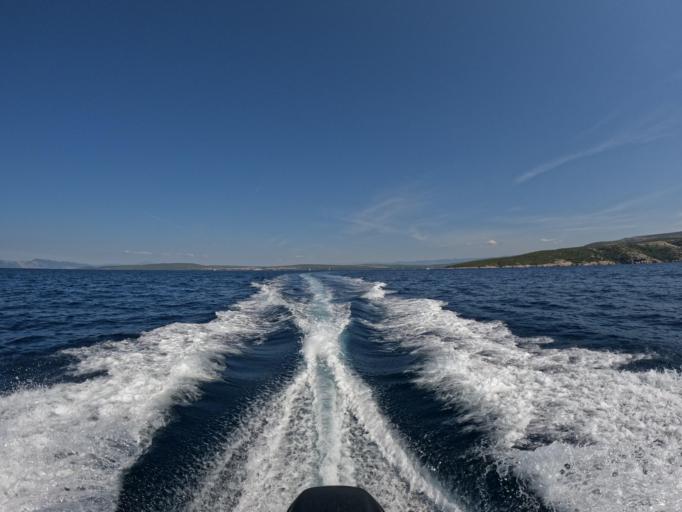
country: HR
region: Primorsko-Goranska
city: Punat
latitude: 44.9645
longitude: 14.6080
